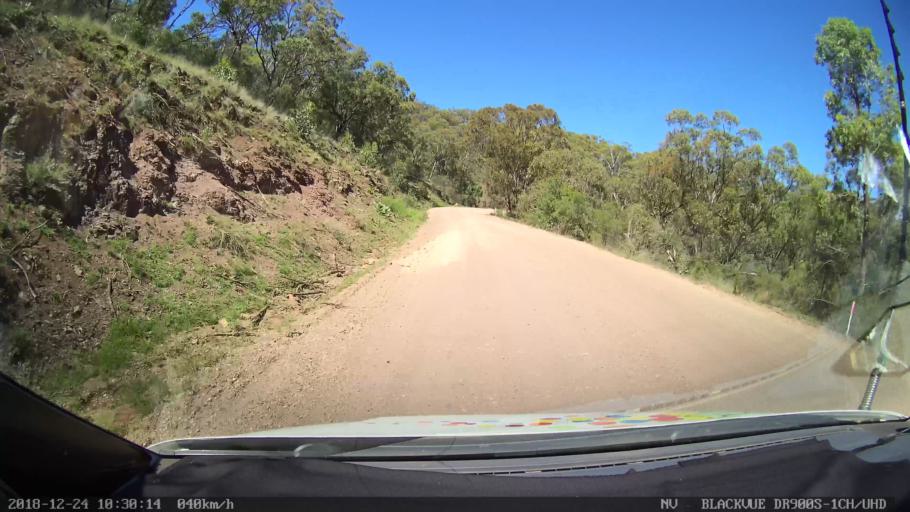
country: AU
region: New South Wales
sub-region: Upper Hunter Shire
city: Merriwa
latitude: -31.8359
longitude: 150.5262
